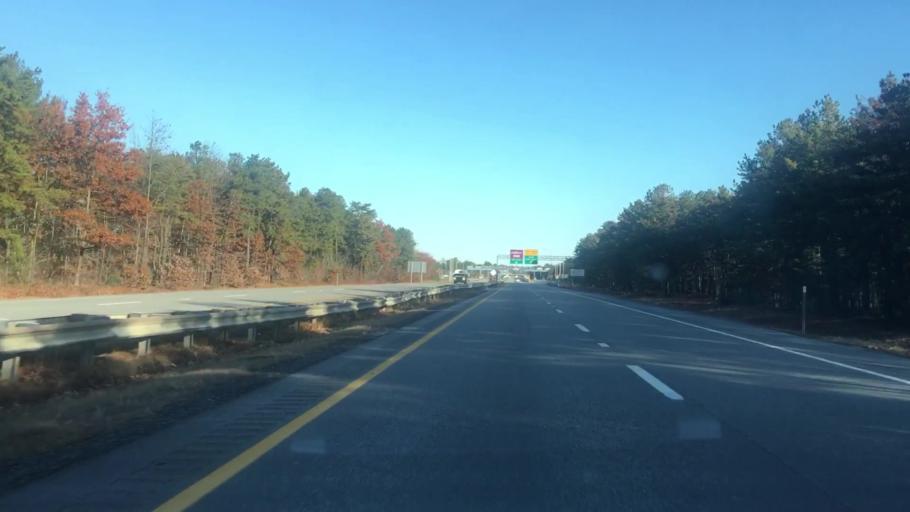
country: US
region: Maine
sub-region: Cumberland County
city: New Gloucester
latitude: 43.9305
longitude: -70.3359
